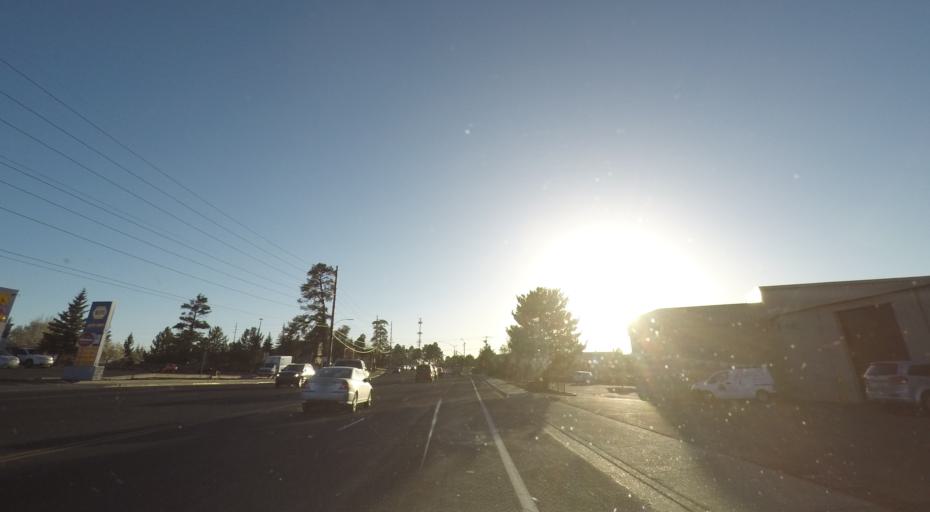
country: US
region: Arizona
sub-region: Coconino County
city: Flagstaff
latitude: 35.1918
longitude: -111.6288
